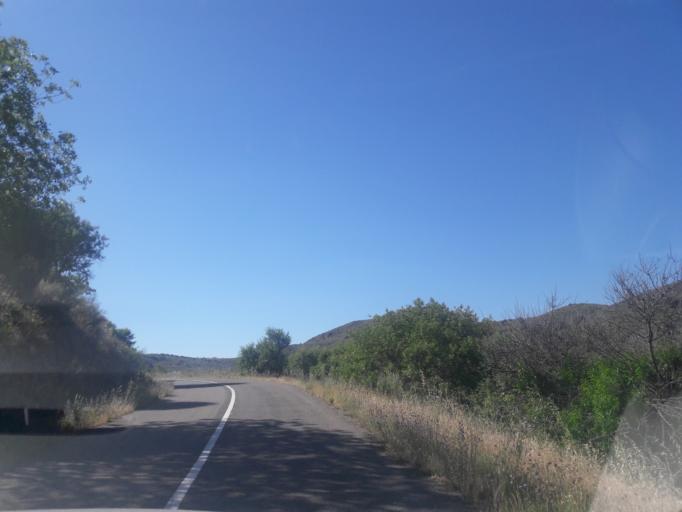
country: ES
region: Castille and Leon
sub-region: Provincia de Salamanca
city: Saucelle
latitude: 41.0197
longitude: -6.7510
